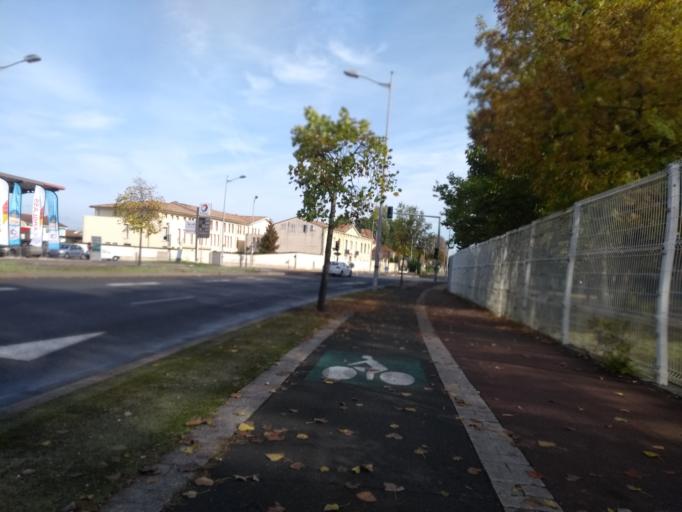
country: FR
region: Aquitaine
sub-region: Departement de la Gironde
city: Talence
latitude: 44.7949
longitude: -0.6042
